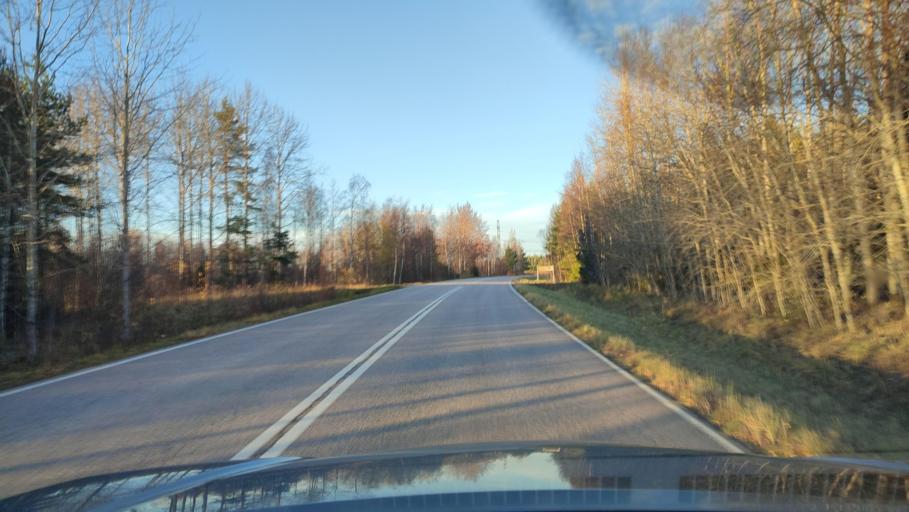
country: FI
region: Ostrobothnia
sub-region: Sydosterbotten
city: Kristinestad
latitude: 62.2885
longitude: 21.3776
